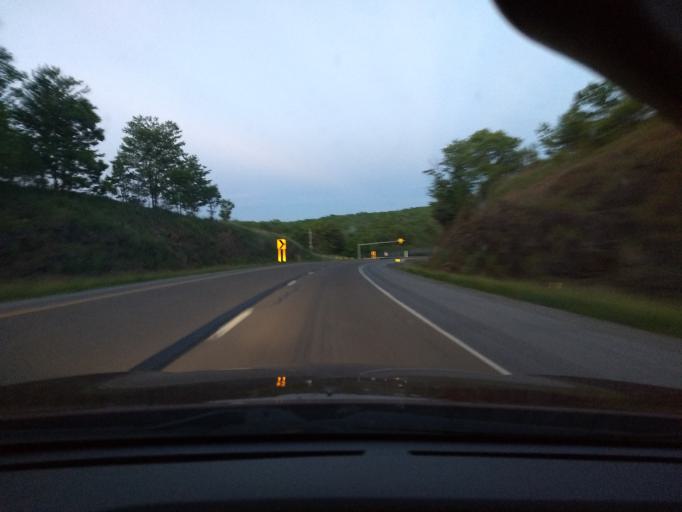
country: US
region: Pennsylvania
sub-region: Lycoming County
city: Jersey Shore
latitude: 41.0631
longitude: -77.2166
